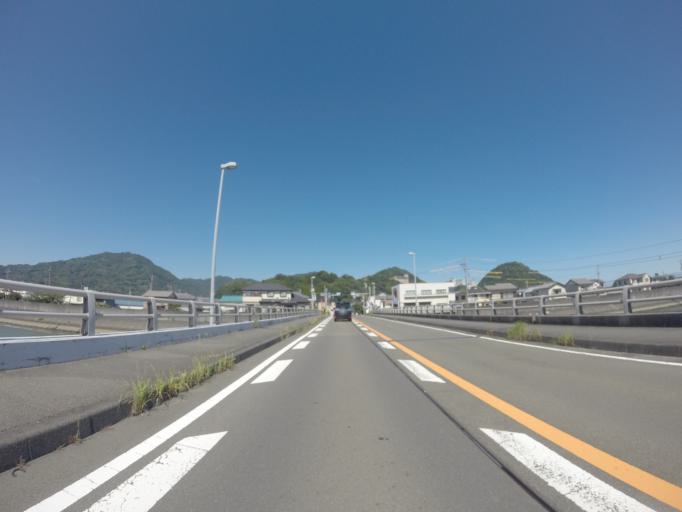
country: JP
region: Shizuoka
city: Yaizu
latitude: 34.8765
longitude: 138.3266
